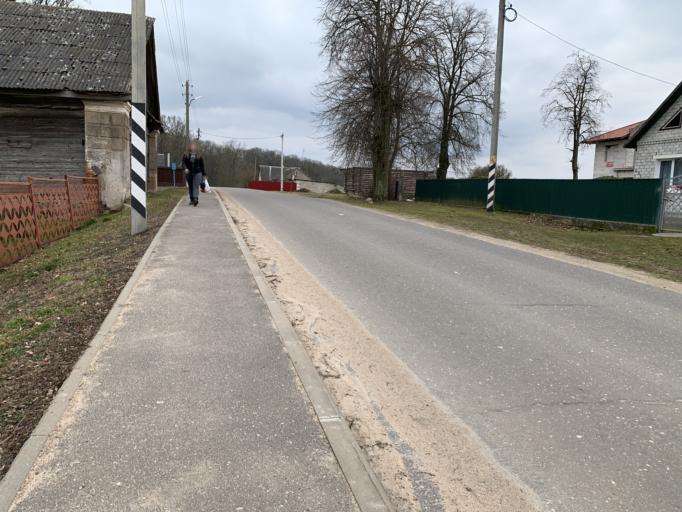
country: BY
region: Minsk
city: Nyasvizh
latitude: 53.2297
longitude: 26.6905
